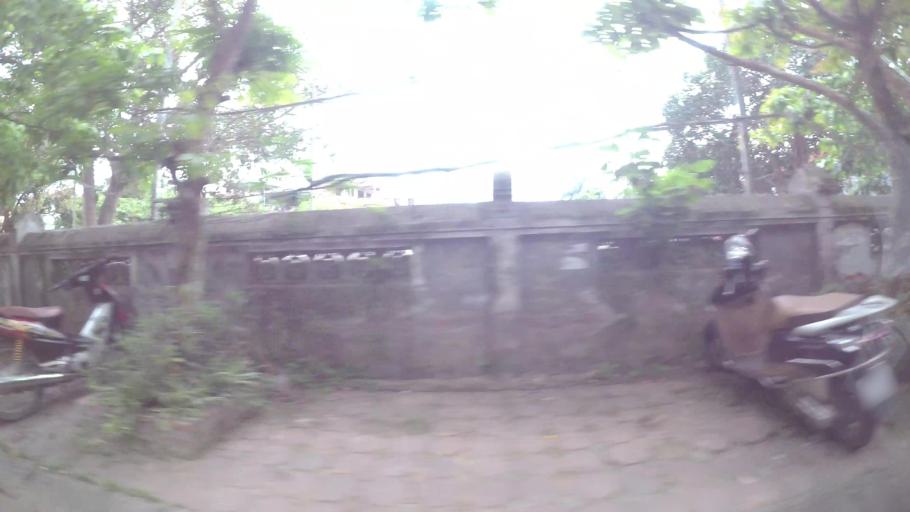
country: VN
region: Ha Noi
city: Trau Quy
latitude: 21.0722
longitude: 105.9178
